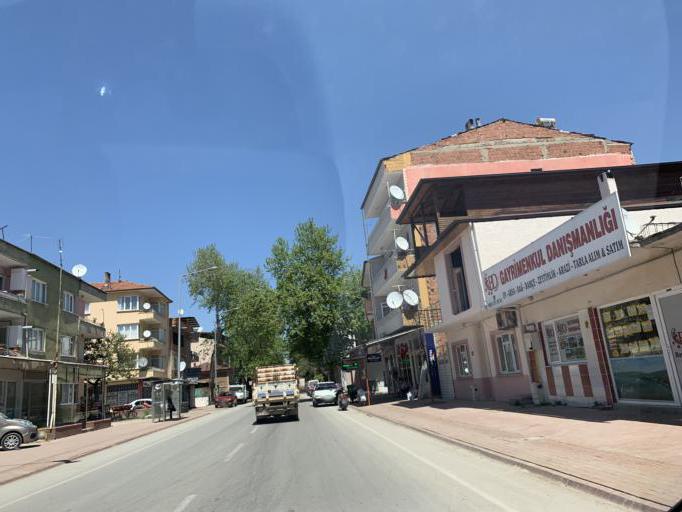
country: TR
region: Bursa
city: Iznik
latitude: 40.4254
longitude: 29.7195
